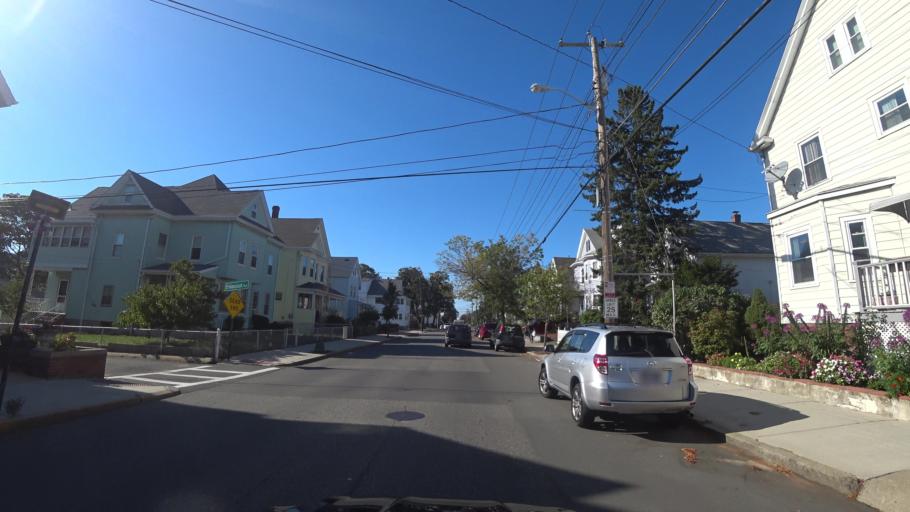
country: US
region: Massachusetts
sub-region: Middlesex County
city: Everett
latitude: 42.4143
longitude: -71.0569
